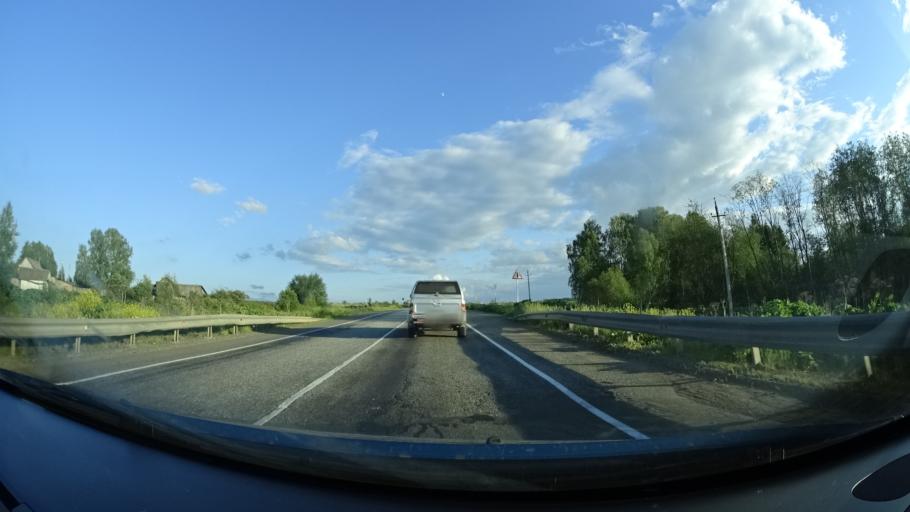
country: RU
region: Perm
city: Osa
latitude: 57.1478
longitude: 55.5292
